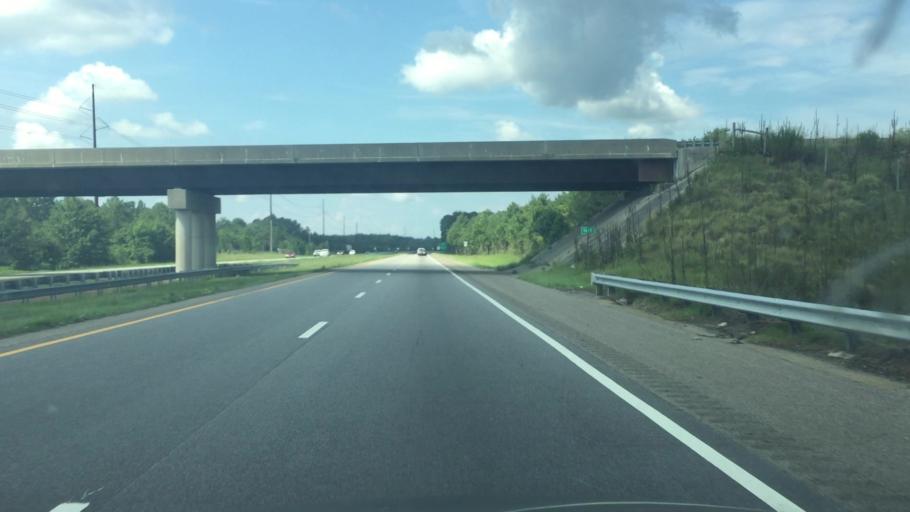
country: US
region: North Carolina
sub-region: Richmond County
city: Hamlet
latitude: 34.8616
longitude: -79.6761
